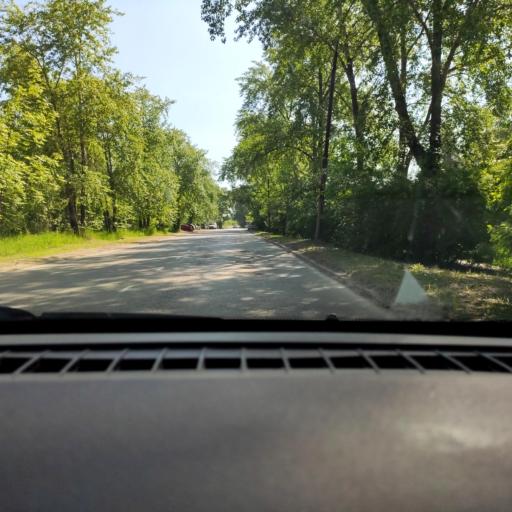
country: RU
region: Perm
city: Overyata
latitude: 57.9948
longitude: 55.8956
